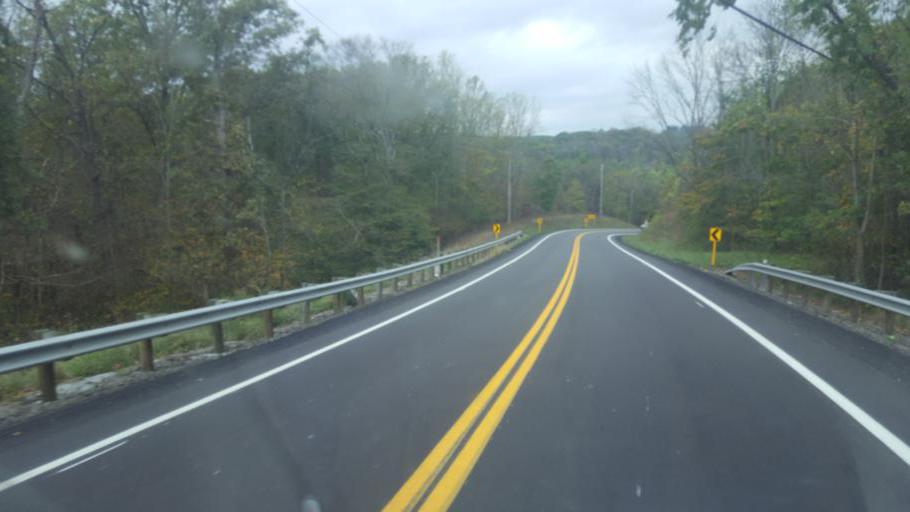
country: US
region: Ohio
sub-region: Carroll County
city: Carrollton
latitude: 40.5083
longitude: -81.1127
